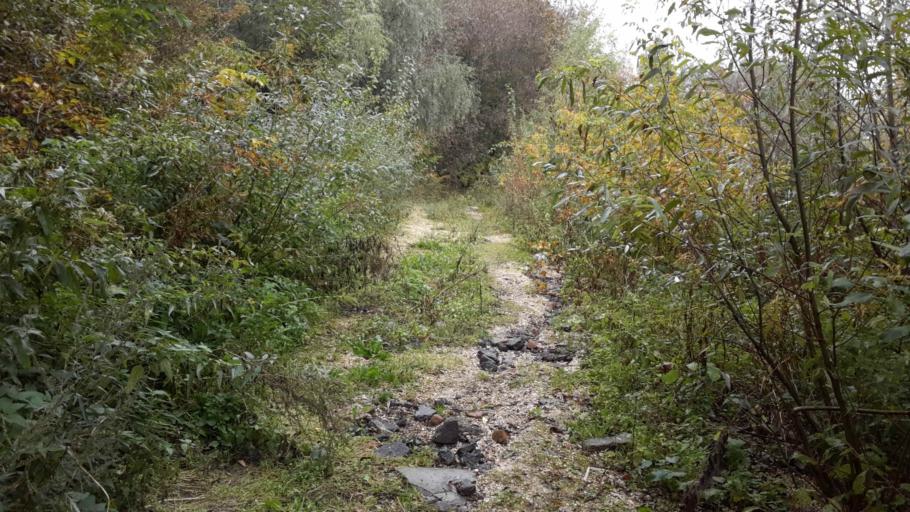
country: RU
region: Moskovskaya
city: Kur'yanovo
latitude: 55.6394
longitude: 37.7032
